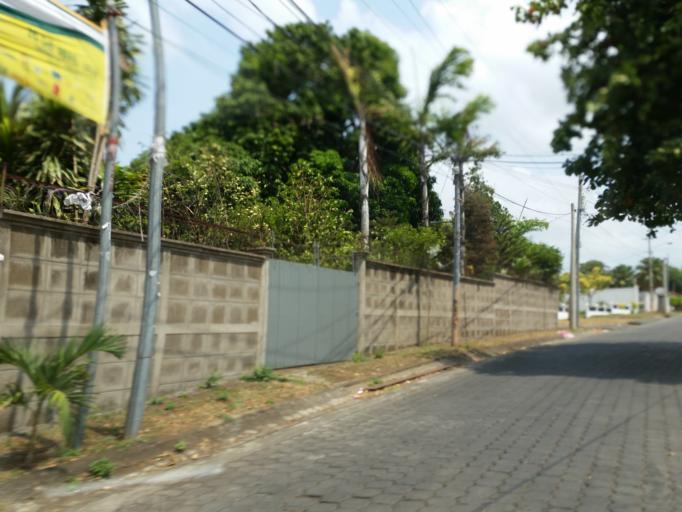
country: NI
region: Managua
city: Managua
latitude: 12.0836
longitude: -86.2319
